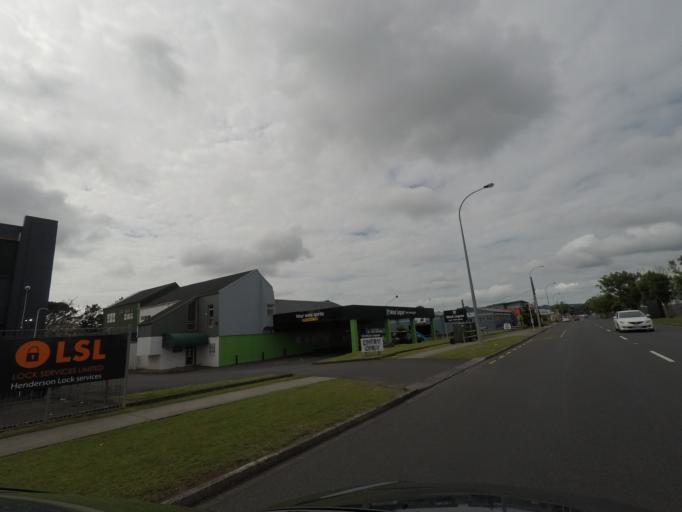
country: NZ
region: Auckland
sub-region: Auckland
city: Waitakere
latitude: -36.8885
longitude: 174.6317
